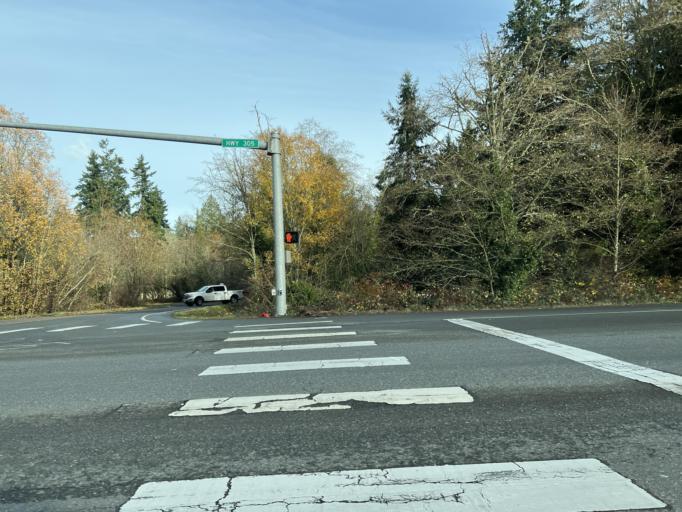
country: US
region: Washington
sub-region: Kitsap County
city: Bainbridge Island
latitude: 47.6443
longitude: -122.5175
